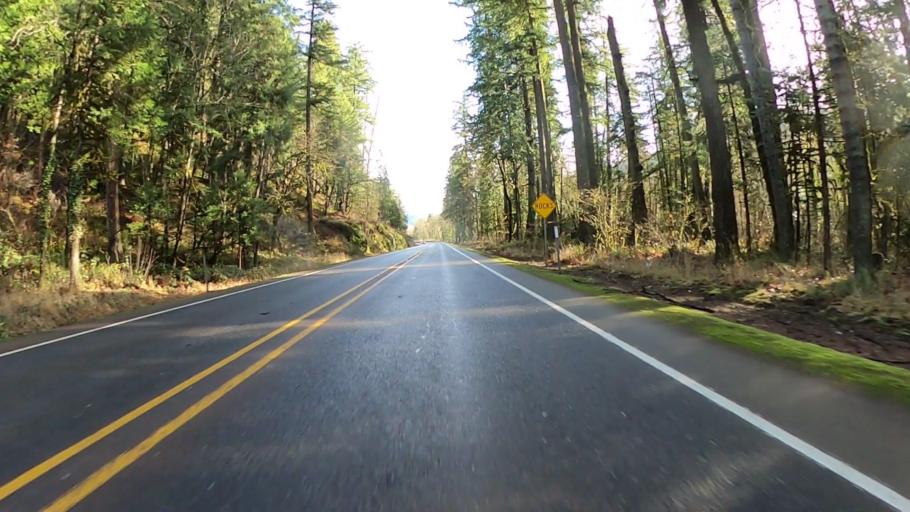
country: US
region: Oregon
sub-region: Lane County
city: Oakridge
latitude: 43.7472
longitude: -122.5018
